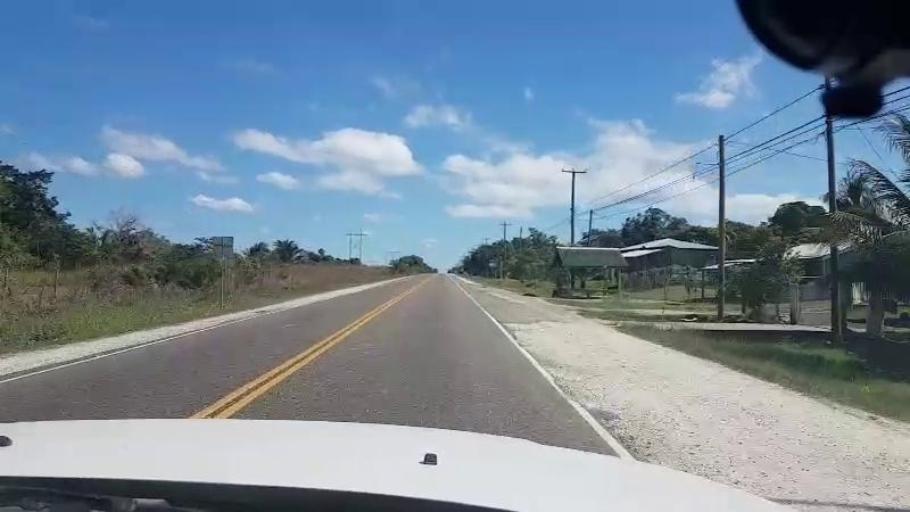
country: BZ
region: Cayo
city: Belmopan
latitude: 17.2768
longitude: -88.7193
